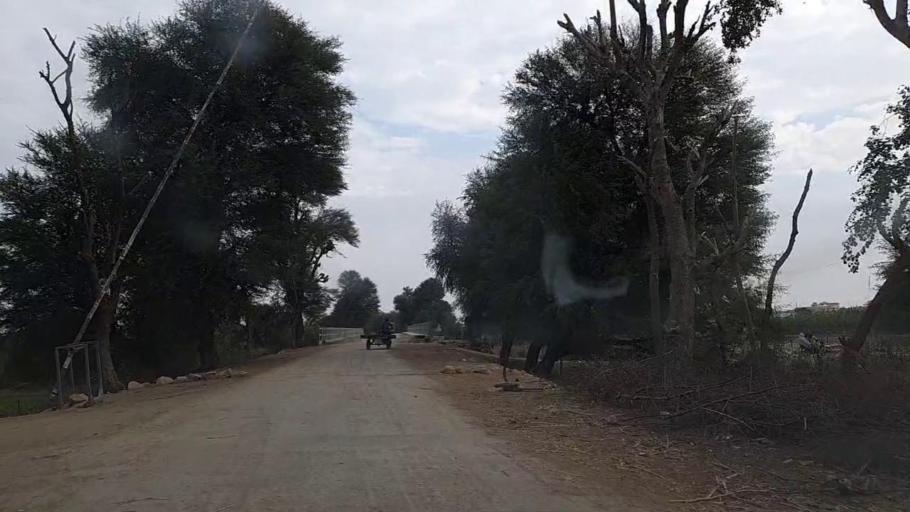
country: PK
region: Sindh
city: Sanghar
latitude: 26.2296
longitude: 68.9979
